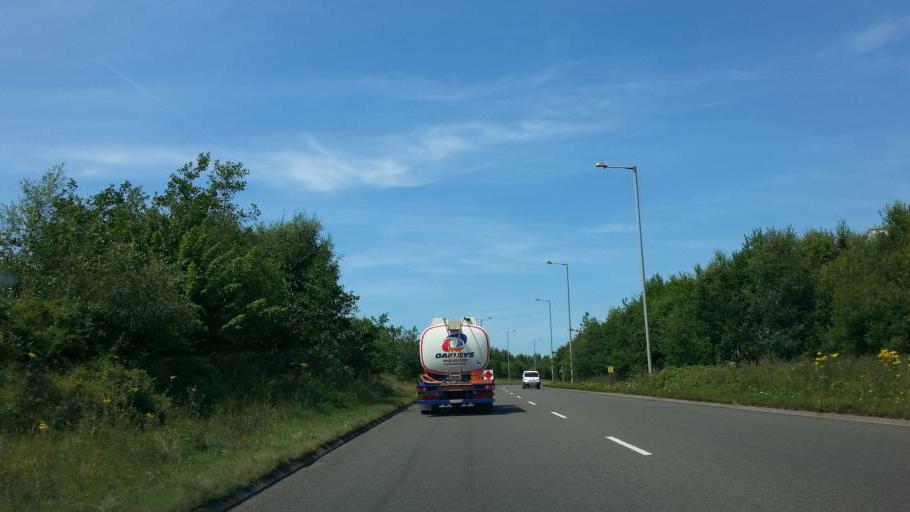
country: GB
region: England
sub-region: Staffordshire
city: Norton Canes
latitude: 52.6789
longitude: -1.9491
